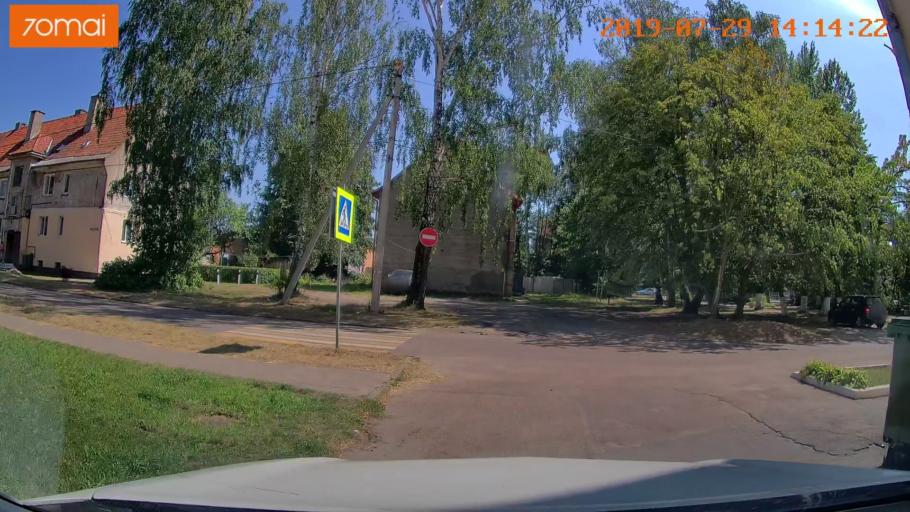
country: RU
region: Kaliningrad
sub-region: Gorod Kaliningrad
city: Baltiysk
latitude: 54.6494
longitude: 19.9020
